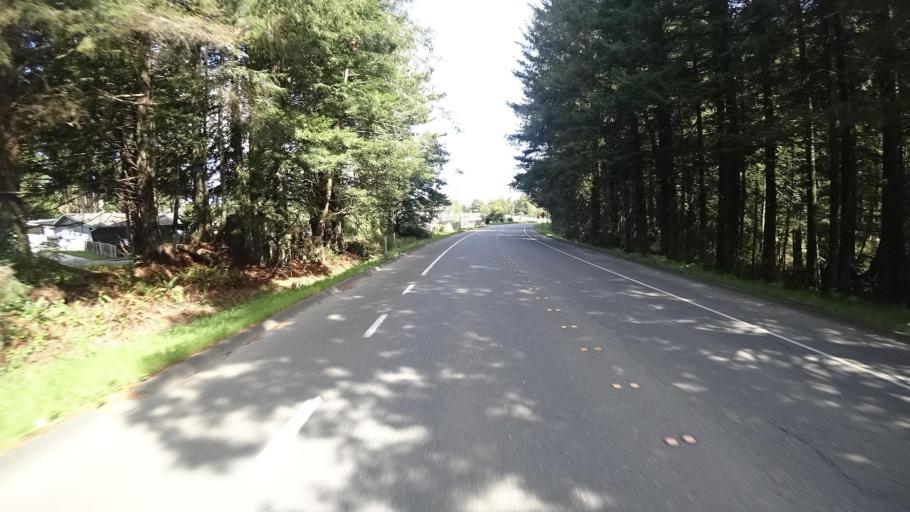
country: US
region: California
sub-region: Humboldt County
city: Cutten
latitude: 40.7559
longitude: -124.1470
